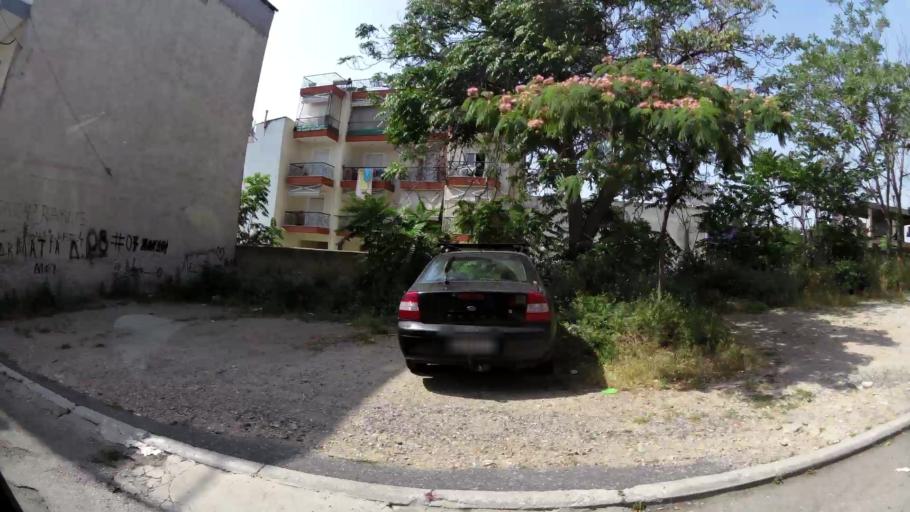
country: GR
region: Central Macedonia
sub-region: Nomos Thessalonikis
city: Stavroupoli
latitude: 40.6725
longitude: 22.9363
